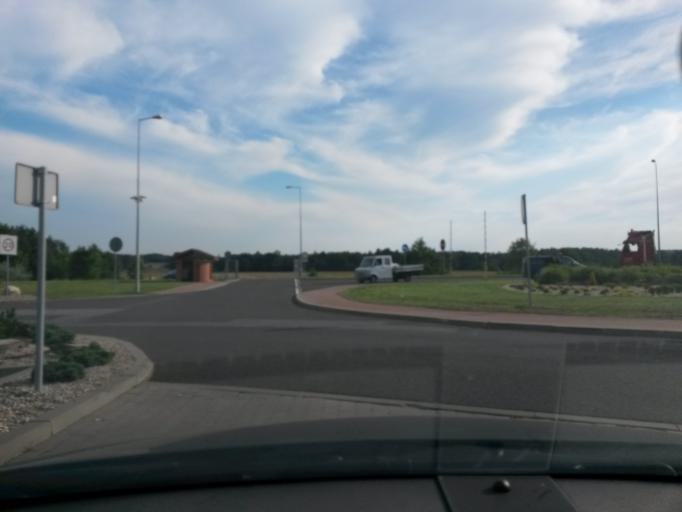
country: PL
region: Greater Poland Voivodeship
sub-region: Powiat turecki
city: Brudzew
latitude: 52.1343
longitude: 18.6337
